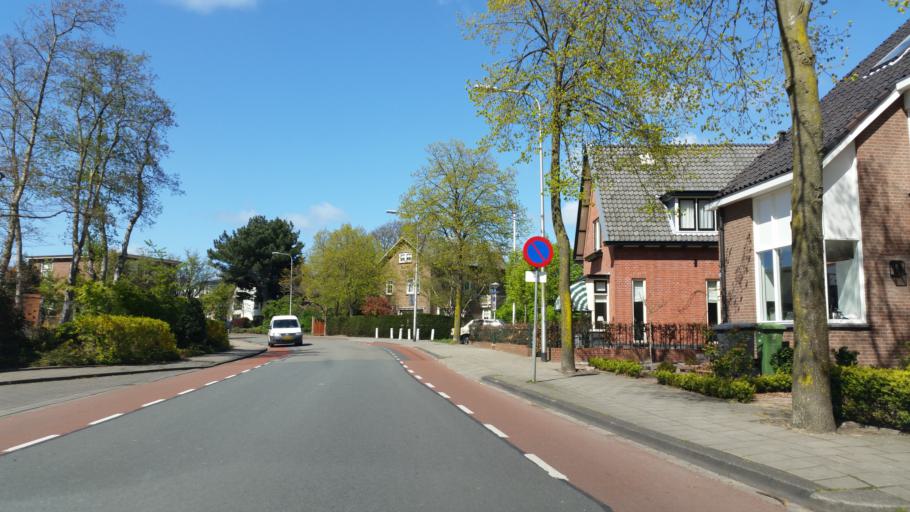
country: NL
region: South Holland
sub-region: Gemeente Katwijk
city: Katwijk aan den Rijn
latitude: 52.1966
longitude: 4.4246
